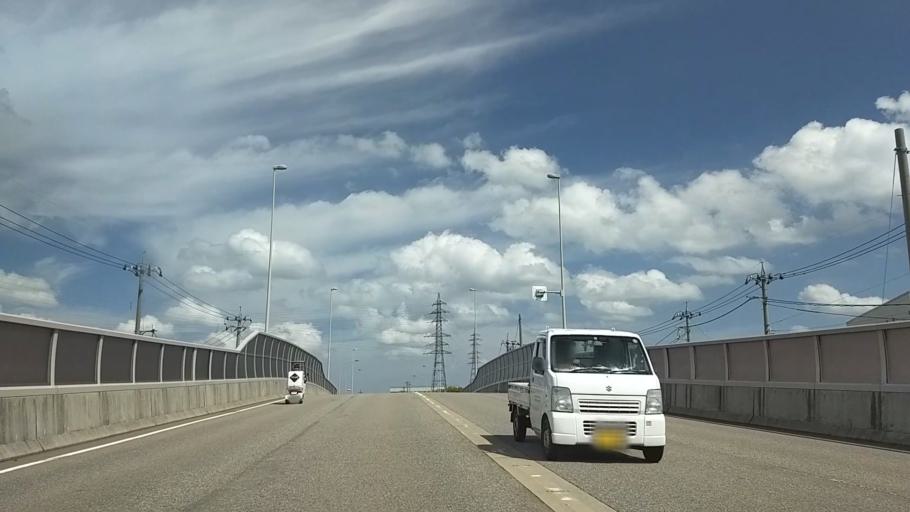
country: JP
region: Ishikawa
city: Kanazawa-shi
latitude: 36.5872
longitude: 136.6491
